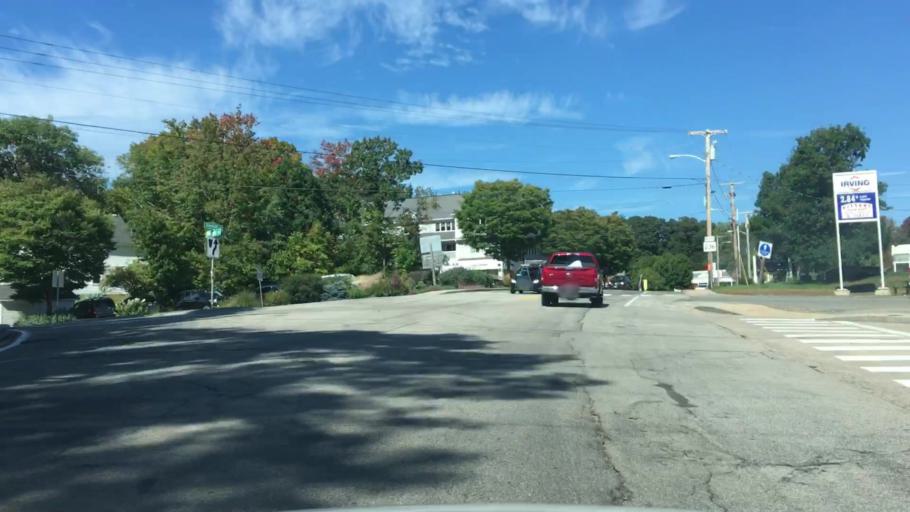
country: US
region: Maine
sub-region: York County
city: Kittery
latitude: 43.0884
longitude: -70.7360
